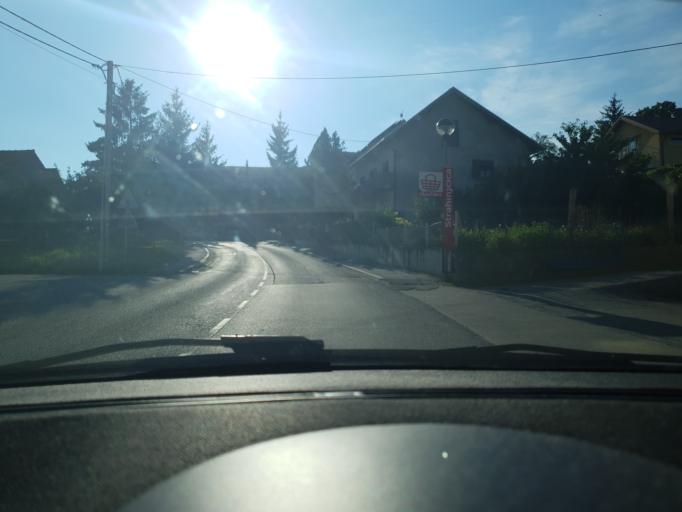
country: HR
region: Krapinsko-Zagorska
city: Radoboj
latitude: 46.1655
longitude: 15.9215
